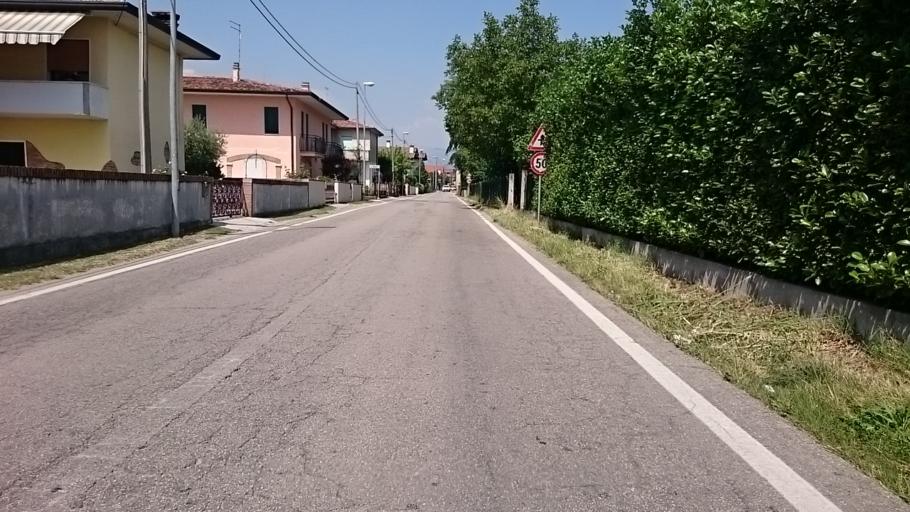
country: IT
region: Veneto
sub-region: Provincia di Vicenza
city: Rosa
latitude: 45.6843
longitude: 11.7401
